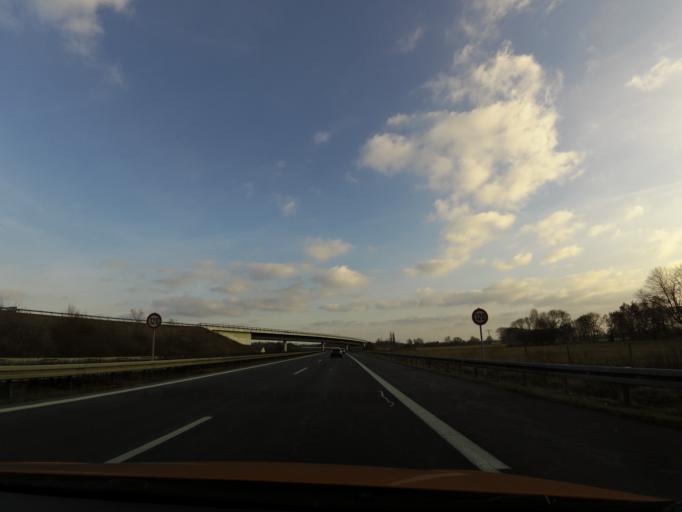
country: DE
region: Brandenburg
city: Leegebruch
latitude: 52.7013
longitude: 13.1968
